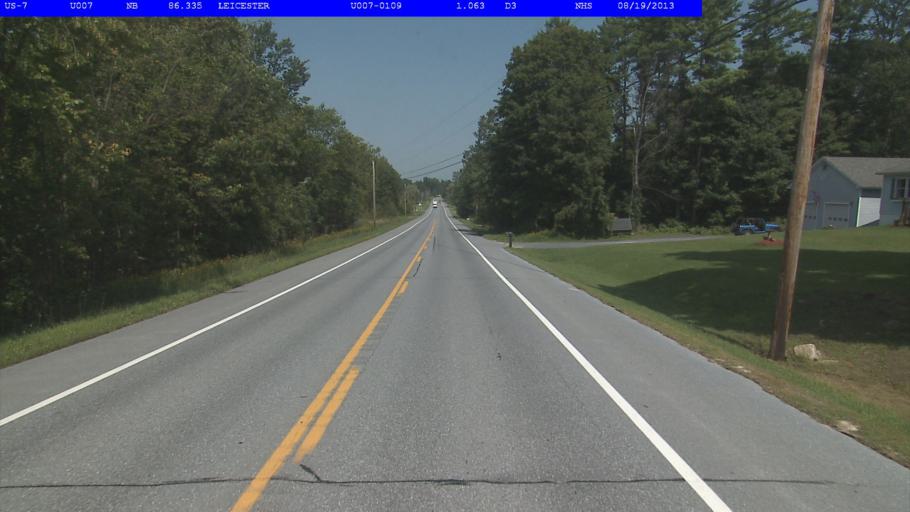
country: US
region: Vermont
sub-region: Rutland County
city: Brandon
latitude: 43.8587
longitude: -73.1063
